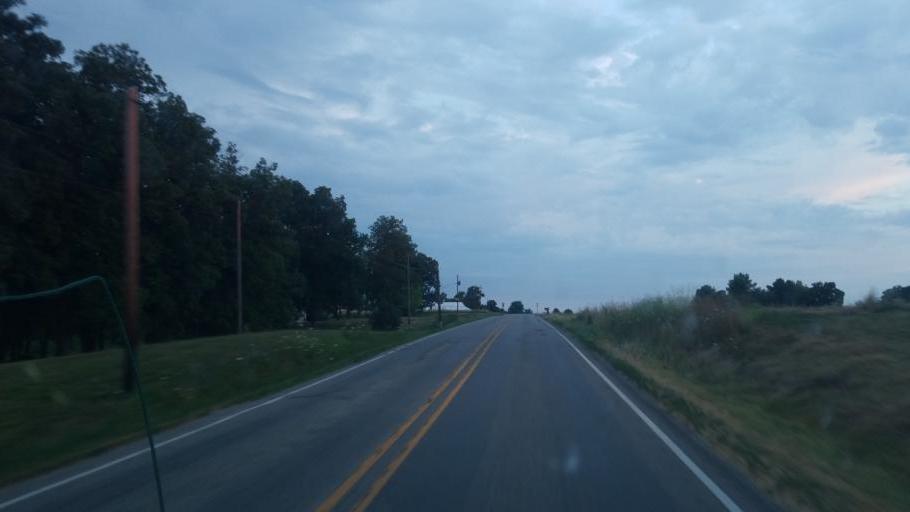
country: US
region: Ohio
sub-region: Defiance County
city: Hicksville
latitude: 41.3325
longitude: -84.8137
